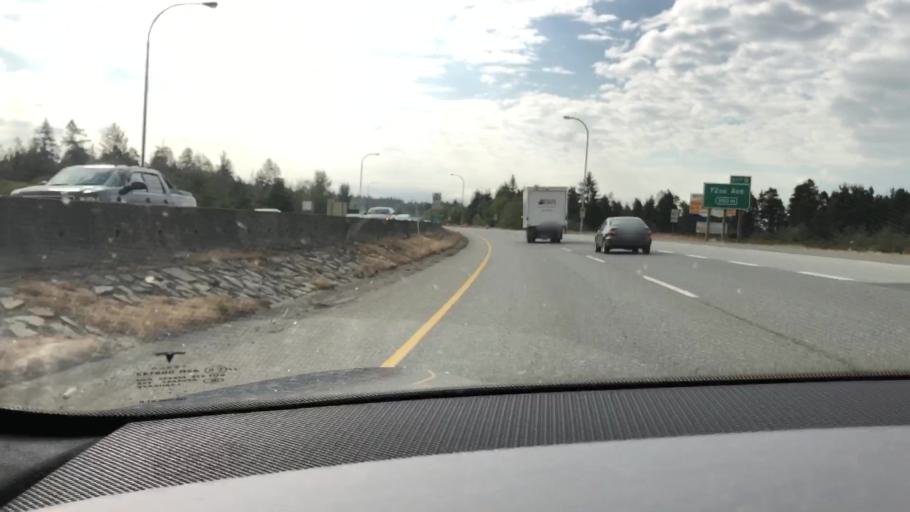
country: CA
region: British Columbia
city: Delta
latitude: 49.1413
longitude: -122.9353
